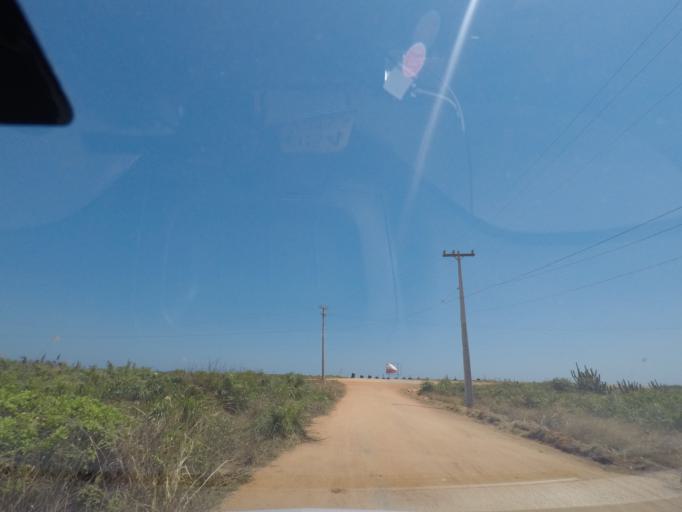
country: BR
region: Rio de Janeiro
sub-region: Marica
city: Marica
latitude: -22.9710
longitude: -42.9450
